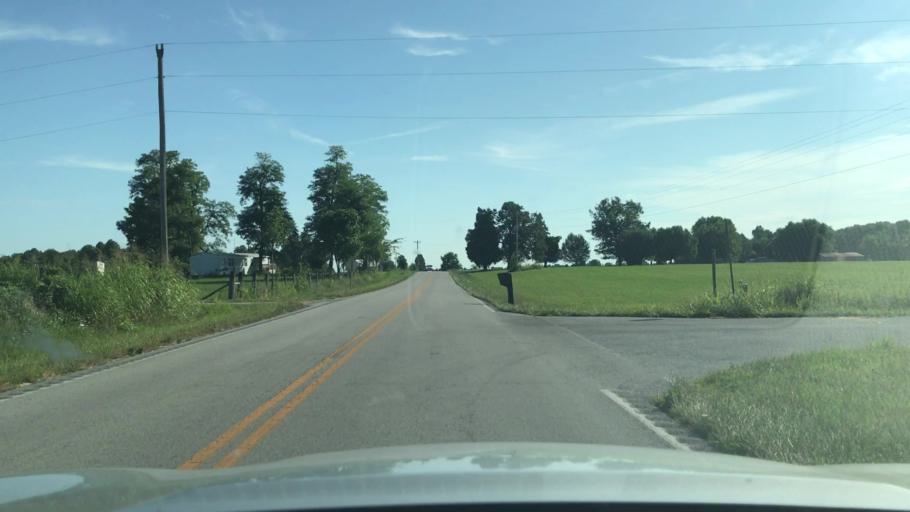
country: US
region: Kentucky
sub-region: Todd County
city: Elkton
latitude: 36.9992
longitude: -87.1349
